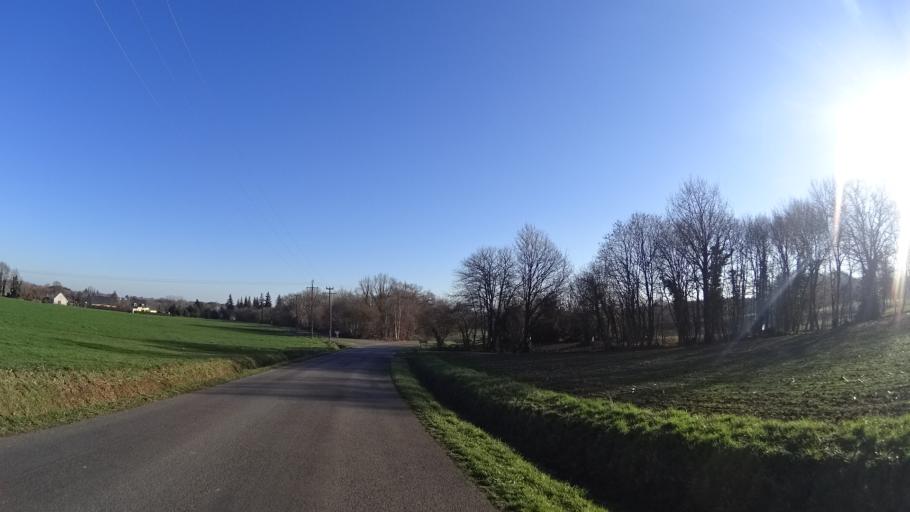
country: FR
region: Brittany
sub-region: Departement du Morbihan
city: Allaire
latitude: 47.6403
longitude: -2.1522
